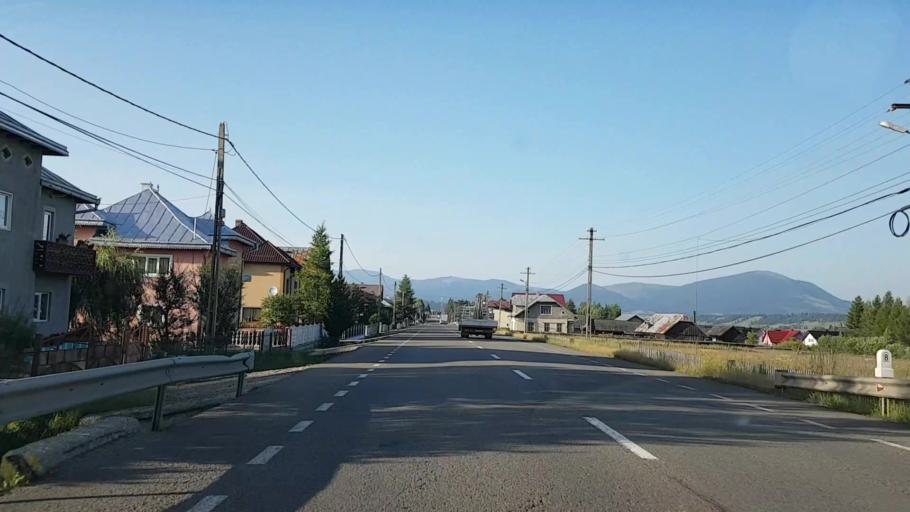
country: RO
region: Suceava
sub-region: Comuna Poiana Stampei
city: Poiana Stampei
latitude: 47.3147
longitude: 25.1318
